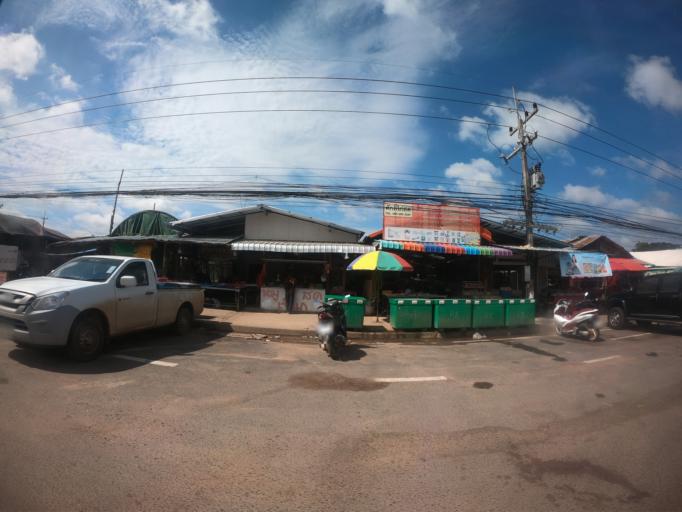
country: TH
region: Surin
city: Kap Choeng
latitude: 14.4531
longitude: 103.6907
